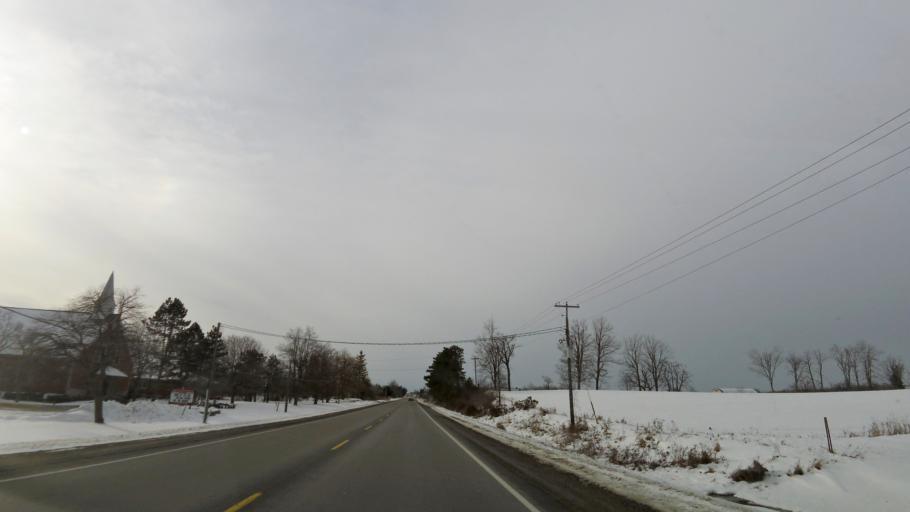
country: CA
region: Ontario
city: Ancaster
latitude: 43.2985
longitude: -79.9654
